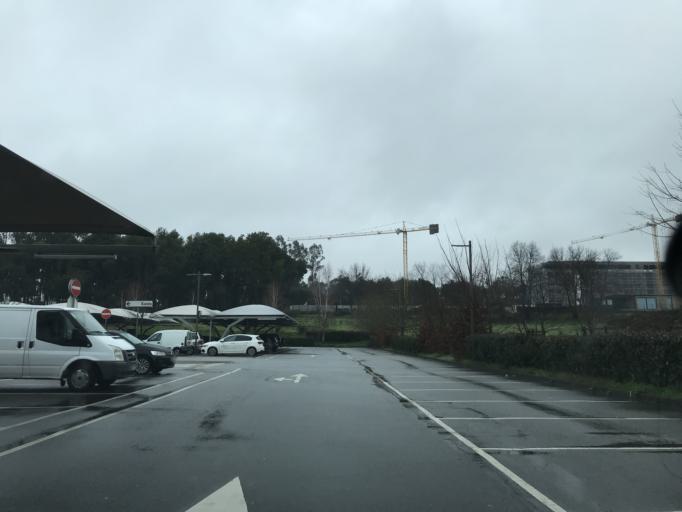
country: PT
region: Braga
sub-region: Vila Nova de Famalicao
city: Vila Nova de Famalicao
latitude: 41.4129
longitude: -8.5112
